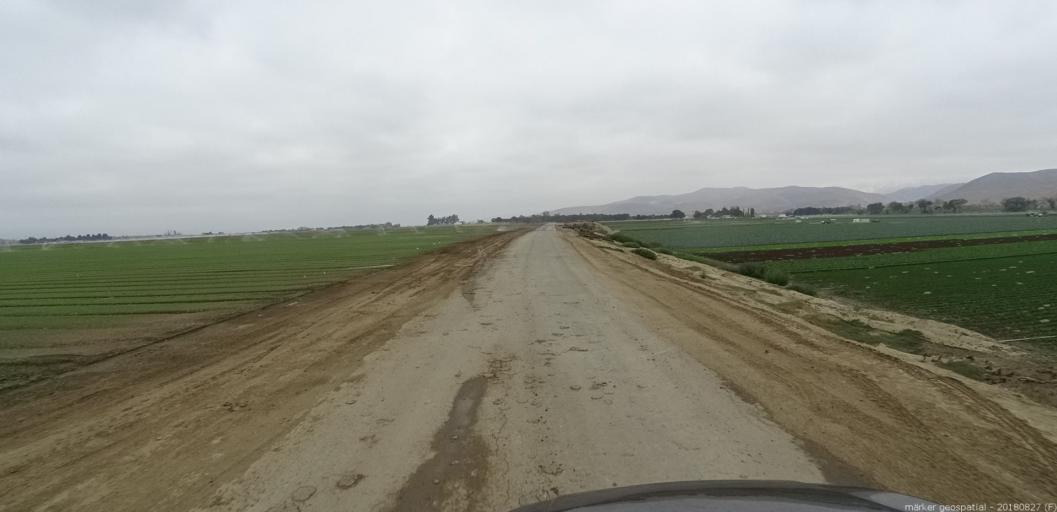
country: US
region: California
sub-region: Monterey County
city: Greenfield
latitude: 36.3231
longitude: -121.2067
